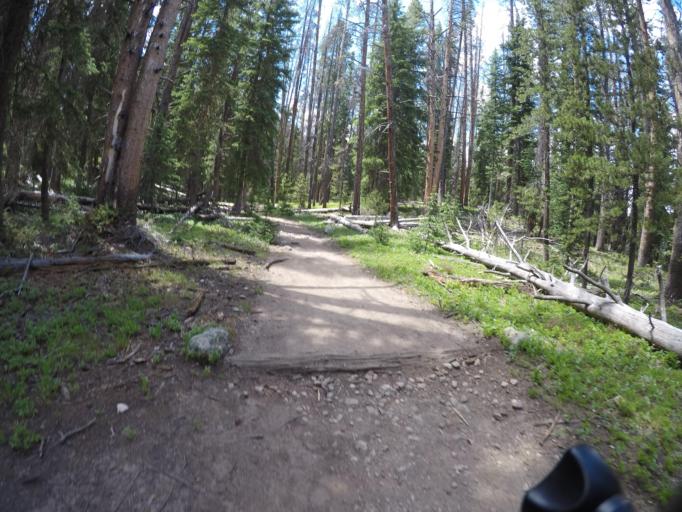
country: US
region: Colorado
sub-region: Grand County
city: Granby
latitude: 40.3106
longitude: -105.8110
